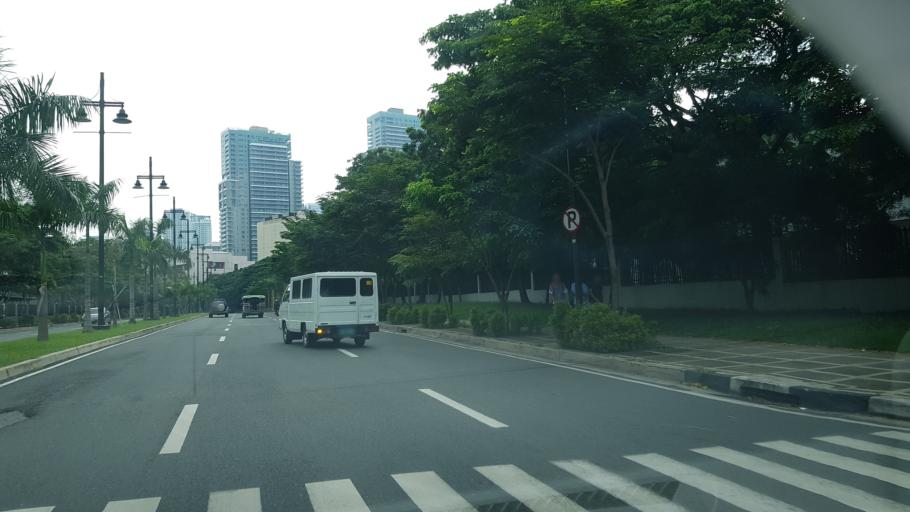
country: PH
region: Calabarzon
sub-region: Province of Rizal
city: Pateros
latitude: 14.5557
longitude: 121.0582
